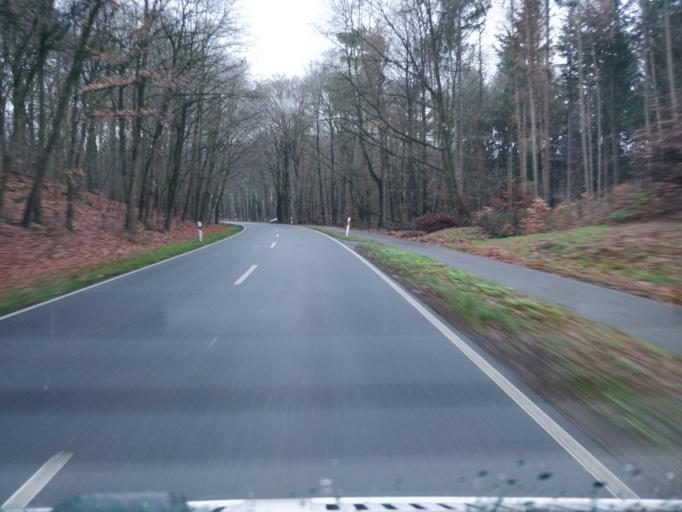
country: DE
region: North Rhine-Westphalia
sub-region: Regierungsbezirk Dusseldorf
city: Mehrhoog
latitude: 51.7652
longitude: 6.4821
